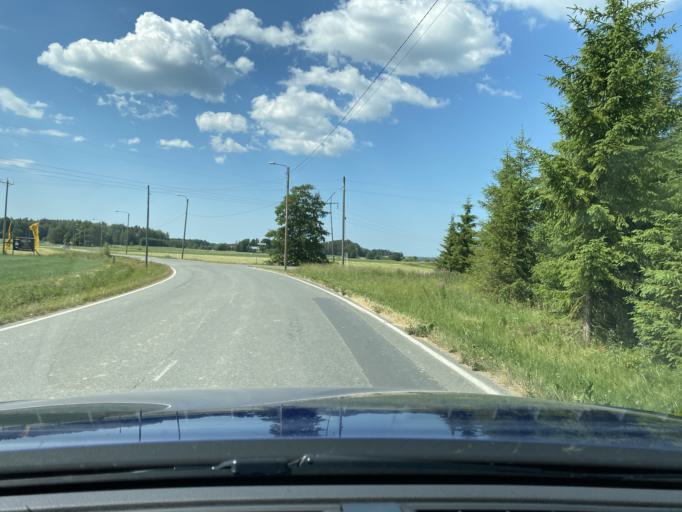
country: FI
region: Satakunta
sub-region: Rauma
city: Eura
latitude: 61.1454
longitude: 22.1114
